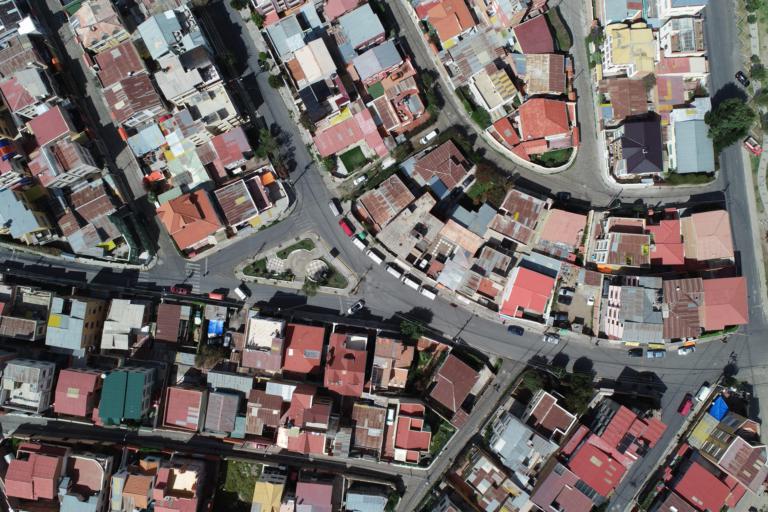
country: BO
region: La Paz
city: La Paz
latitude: -16.5202
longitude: -68.1034
